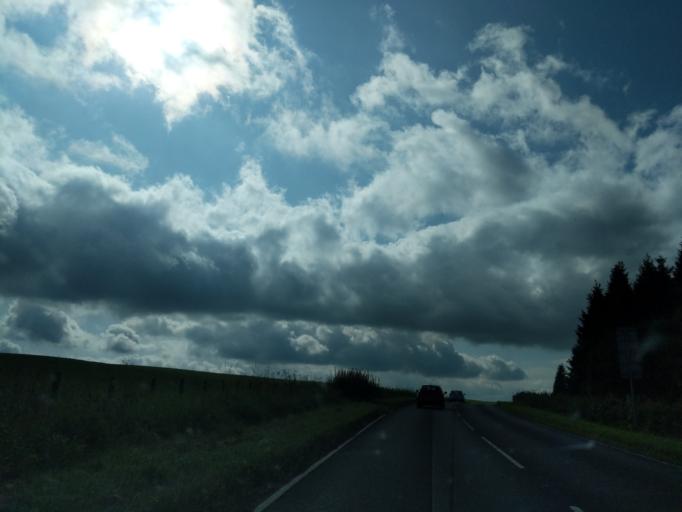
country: GB
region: Scotland
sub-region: Midlothian
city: Penicuik
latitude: 55.7830
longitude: -3.2193
